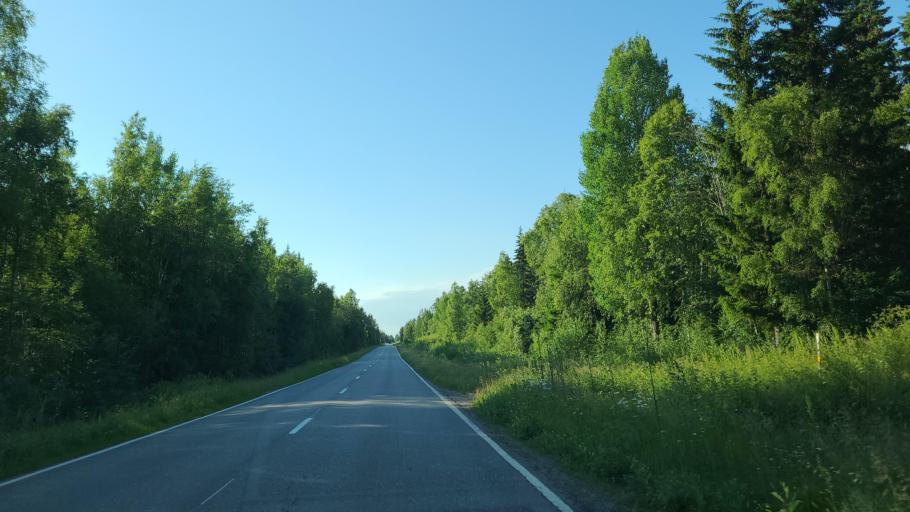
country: FI
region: Ostrobothnia
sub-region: Vaasa
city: Replot
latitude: 63.2514
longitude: 21.3732
